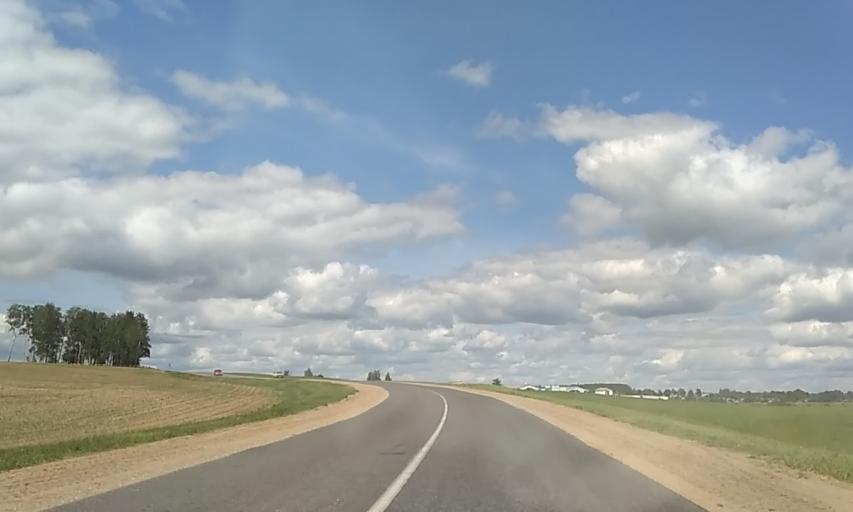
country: BY
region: Minsk
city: Krupki
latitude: 54.3405
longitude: 29.1043
